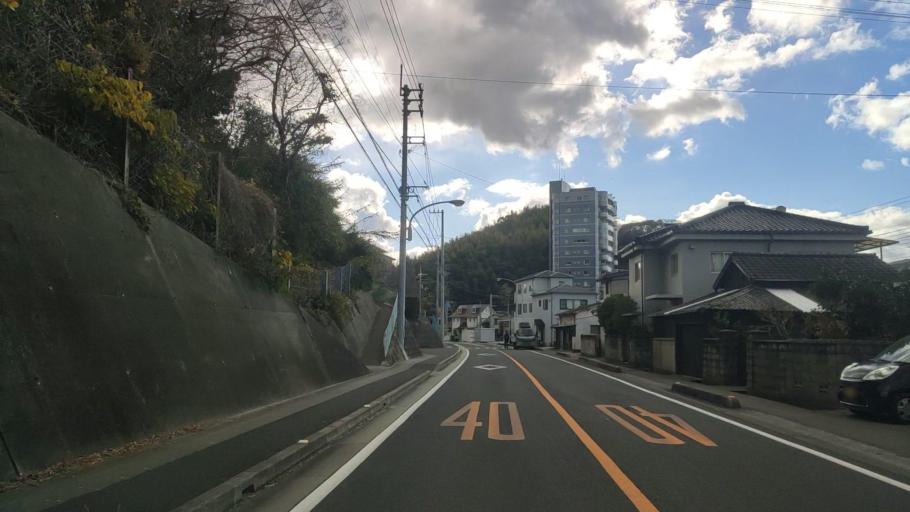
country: JP
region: Ehime
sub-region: Shikoku-chuo Shi
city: Matsuyama
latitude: 33.8713
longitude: 132.7101
